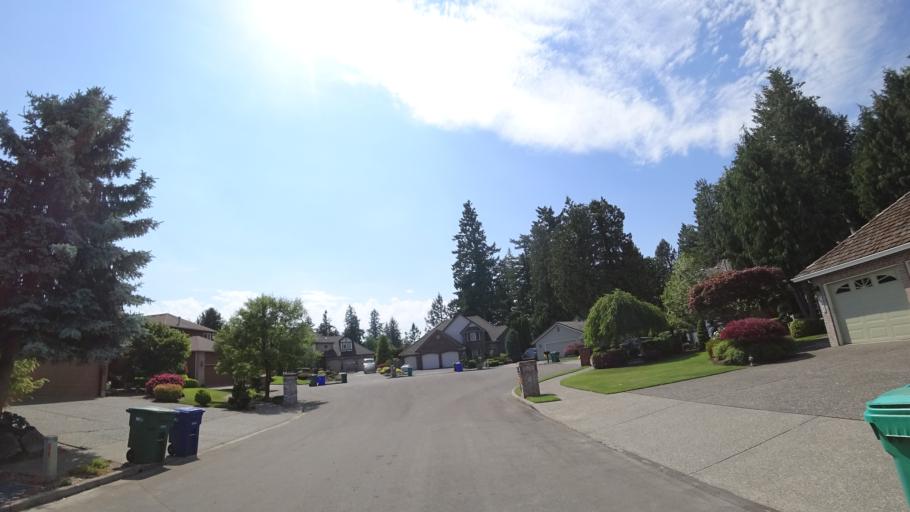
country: US
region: Oregon
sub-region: Multnomah County
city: Fairview
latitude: 45.5400
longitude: -122.4936
